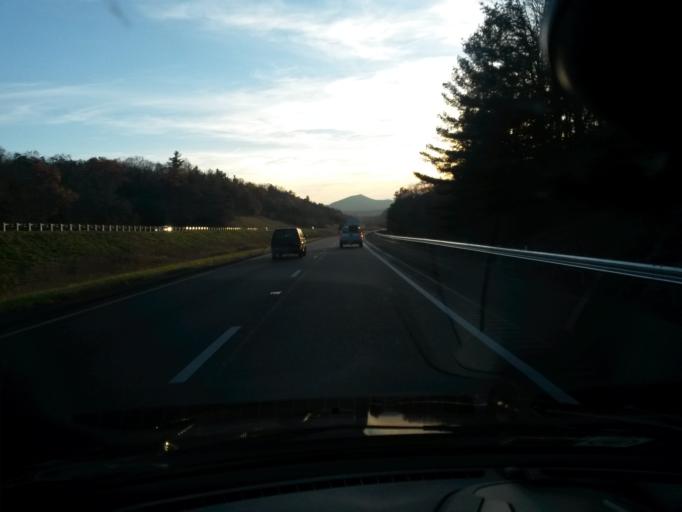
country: US
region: Virginia
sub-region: Alleghany County
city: Clifton Forge
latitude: 37.8411
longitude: -79.6412
